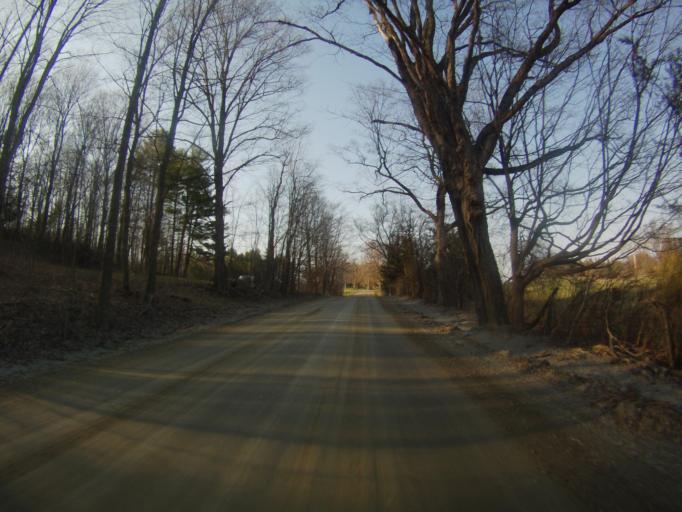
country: US
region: Vermont
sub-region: Addison County
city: Middlebury (village)
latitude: 44.0415
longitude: -73.1469
